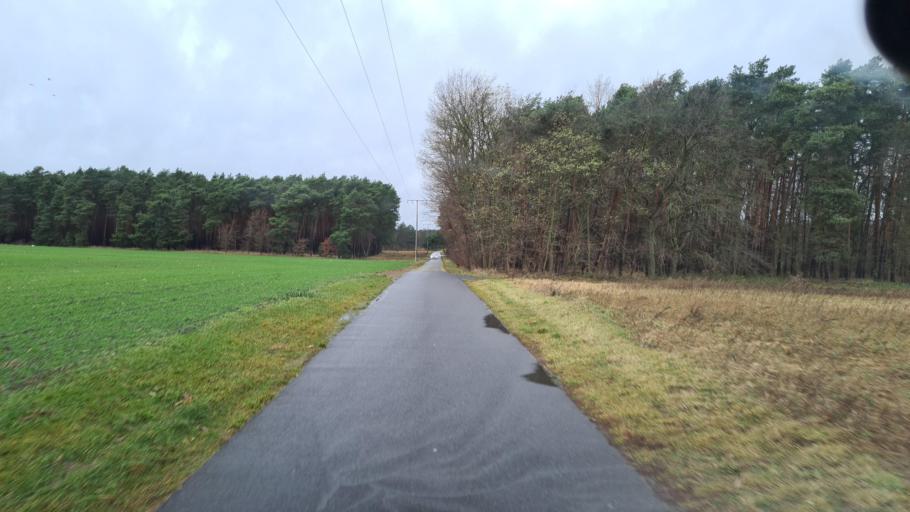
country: DE
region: Brandenburg
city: Tauche
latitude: 52.0874
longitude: 14.1452
